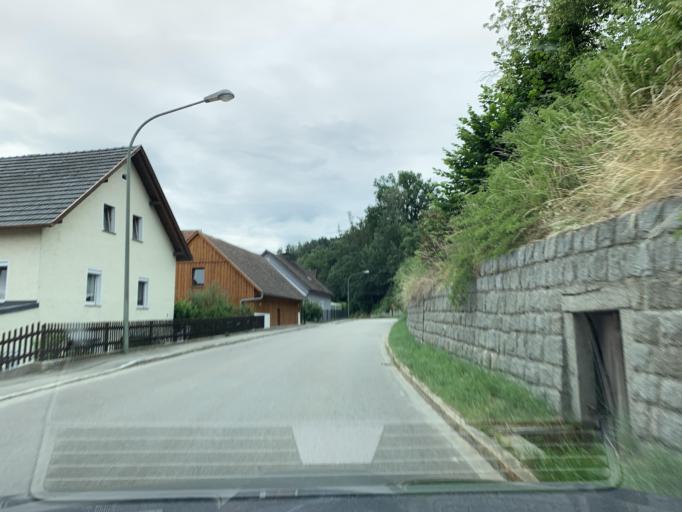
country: DE
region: Bavaria
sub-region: Upper Palatinate
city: Pettendorf
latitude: 49.3518
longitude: 12.3628
